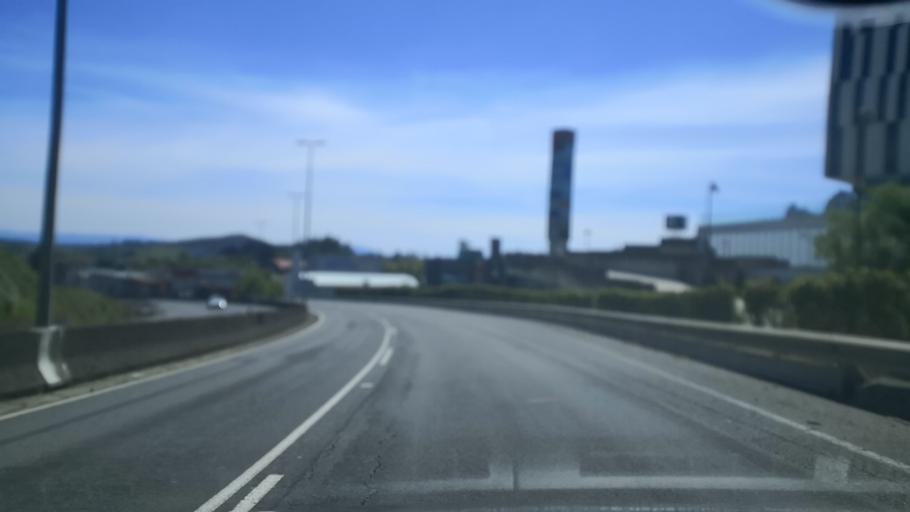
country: ES
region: Galicia
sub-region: Provincia da Coruna
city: Santiago de Compostela
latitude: 42.9046
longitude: -8.5119
